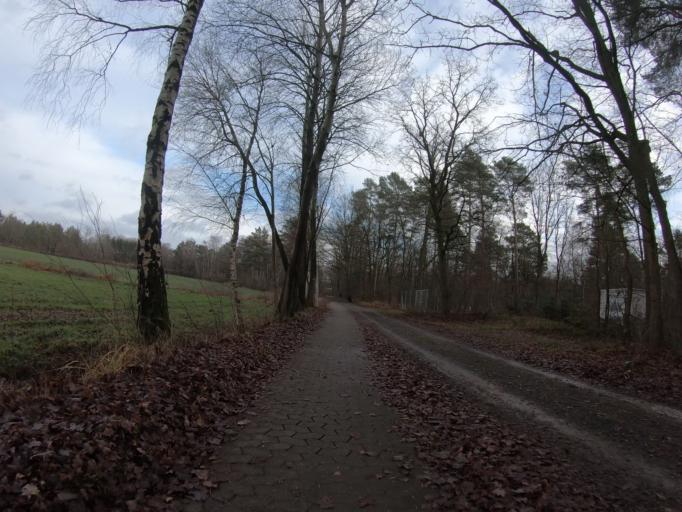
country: DE
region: Lower Saxony
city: Gifhorn
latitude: 52.4903
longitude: 10.5139
